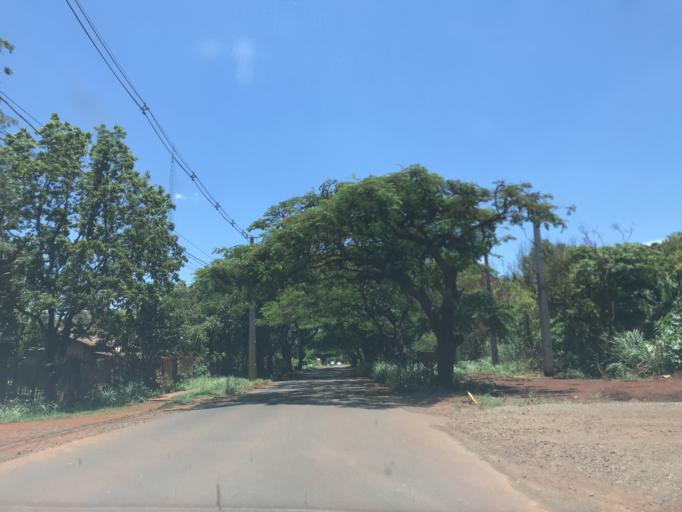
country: BR
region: Parana
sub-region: Sarandi
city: Sarandi
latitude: -23.4425
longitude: -51.9057
